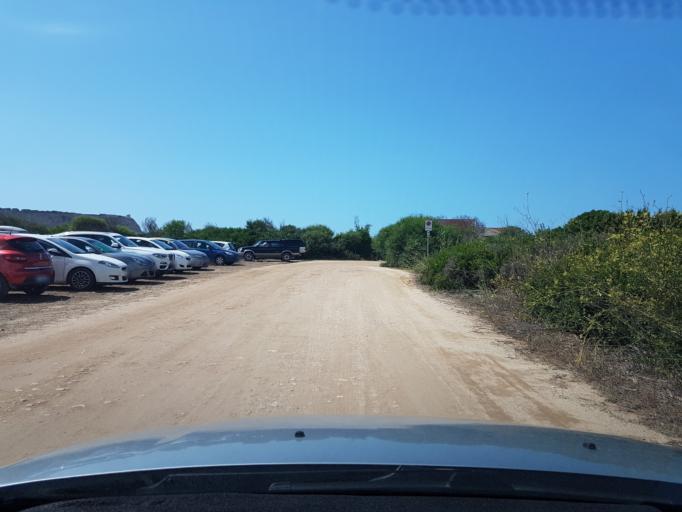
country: IT
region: Sardinia
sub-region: Provincia di Oristano
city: Riola Sardo
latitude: 40.0426
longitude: 8.4017
